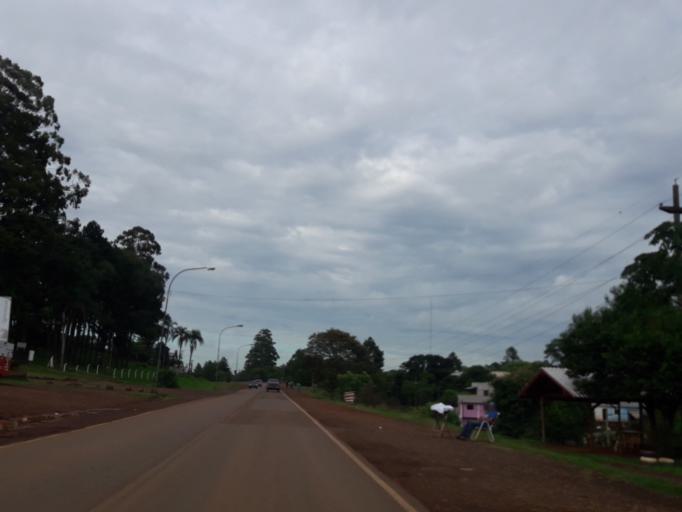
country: AR
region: Misiones
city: Bernardo de Irigoyen
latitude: -26.2621
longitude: -53.6507
